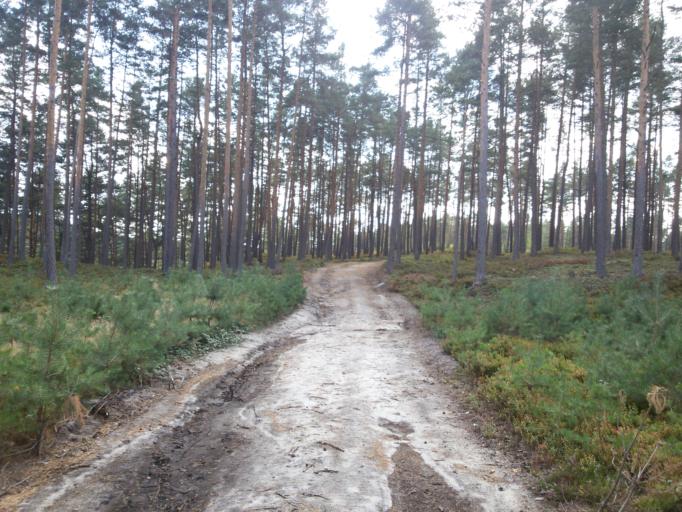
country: CZ
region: Pardubicky
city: Prosec
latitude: 49.8205
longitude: 16.1388
